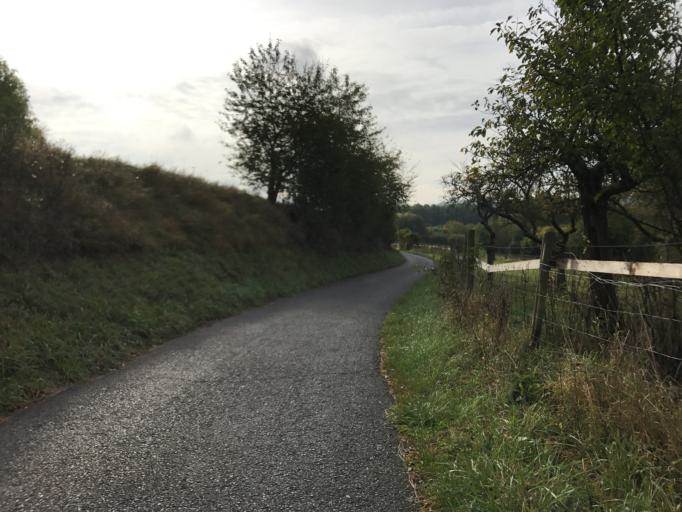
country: DE
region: Rheinland-Pfalz
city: Schwabenheim
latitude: 49.9367
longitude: 8.0832
